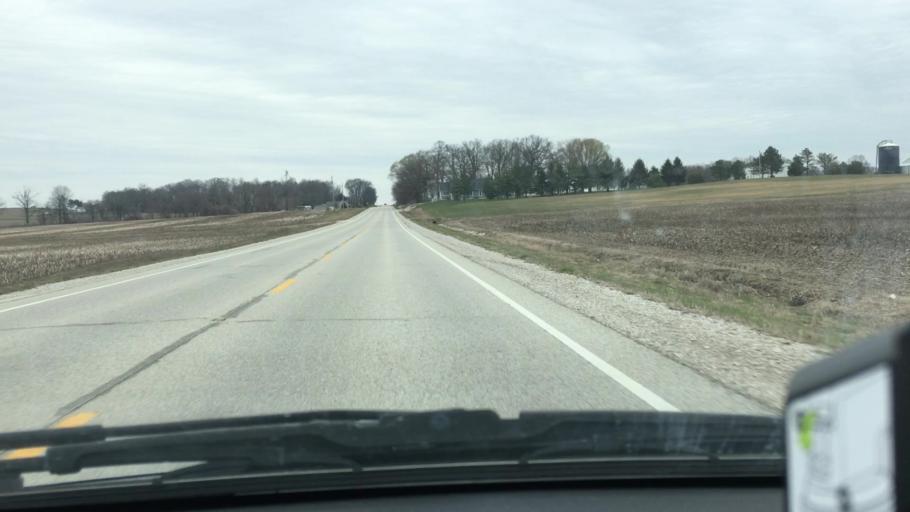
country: US
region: Indiana
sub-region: Greene County
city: Bloomfield
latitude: 38.9869
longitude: -87.0163
